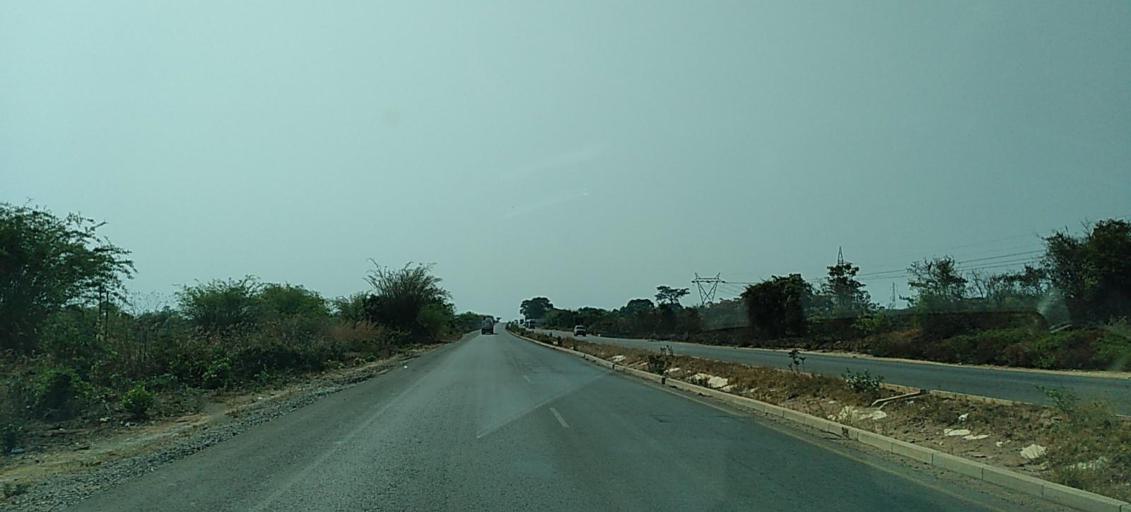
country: ZM
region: Copperbelt
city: Chingola
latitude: -12.5767
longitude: 27.9203
